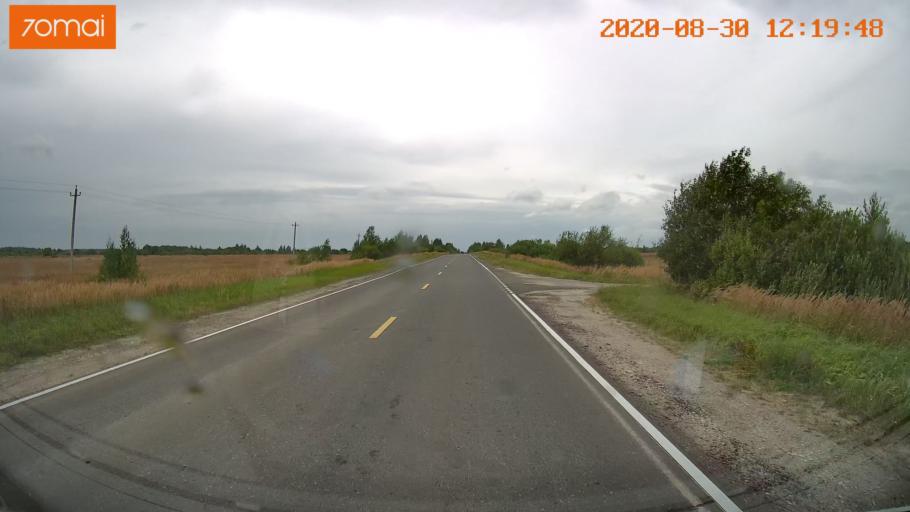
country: RU
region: Ivanovo
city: Yur'yevets
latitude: 57.3230
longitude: 42.9181
